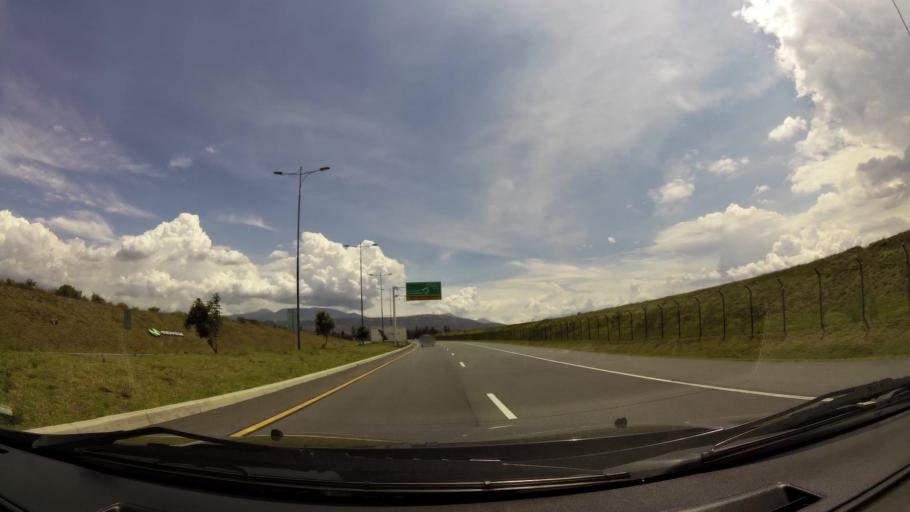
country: EC
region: Pichincha
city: Quito
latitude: -0.1506
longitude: -78.3519
